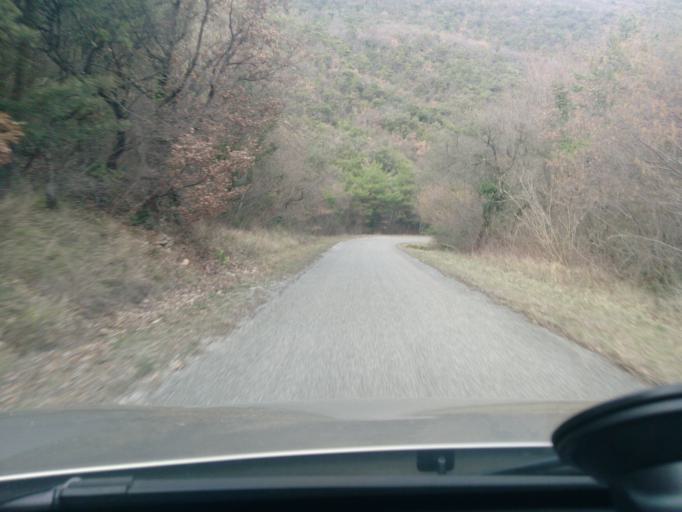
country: FR
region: Rhone-Alpes
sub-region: Departement de l'Ardeche
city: Cruas
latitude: 44.6632
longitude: 4.7430
